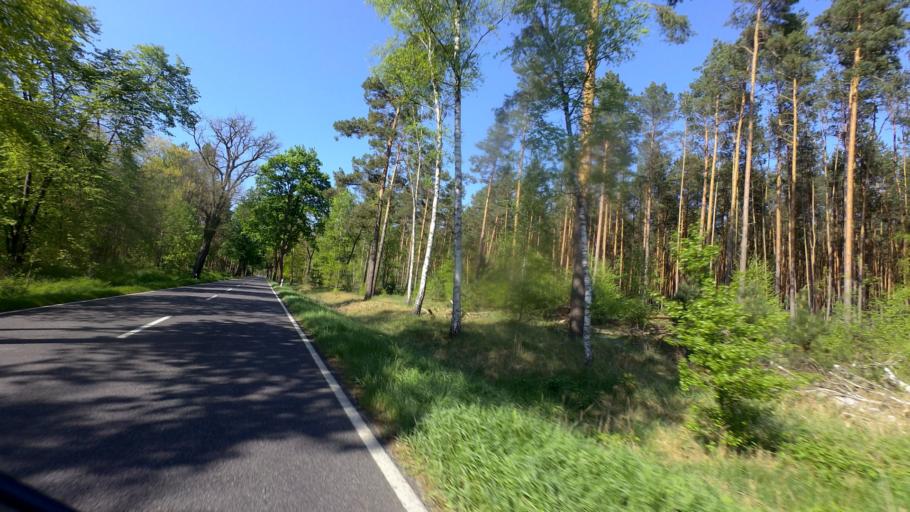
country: DE
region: Brandenburg
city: Halbe
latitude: 52.1454
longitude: 13.7466
